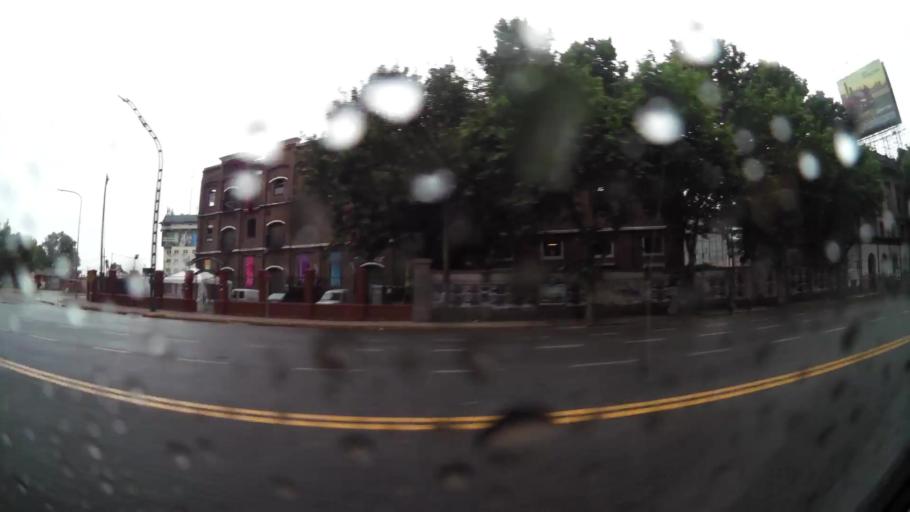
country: AR
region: Buenos Aires F.D.
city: Retiro
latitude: -34.5902
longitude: -58.3789
